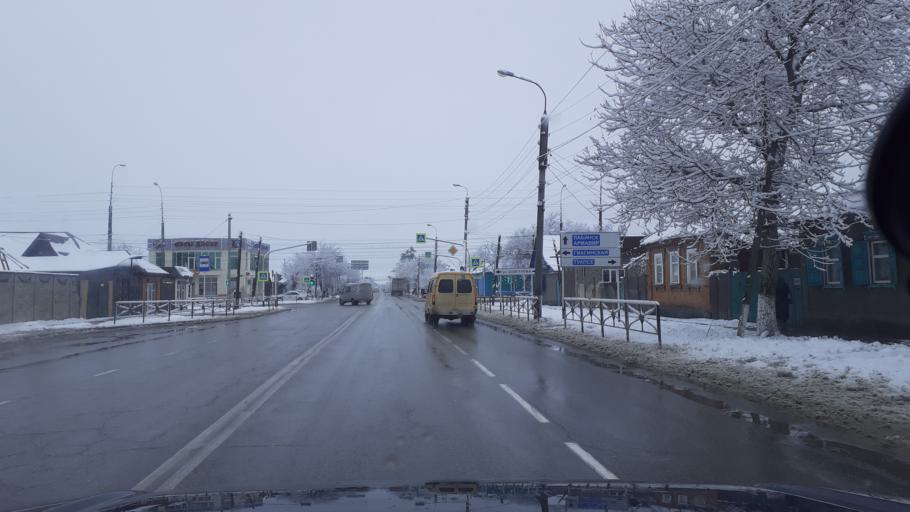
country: RU
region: Adygeya
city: Maykop
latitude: 44.6161
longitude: 40.1197
